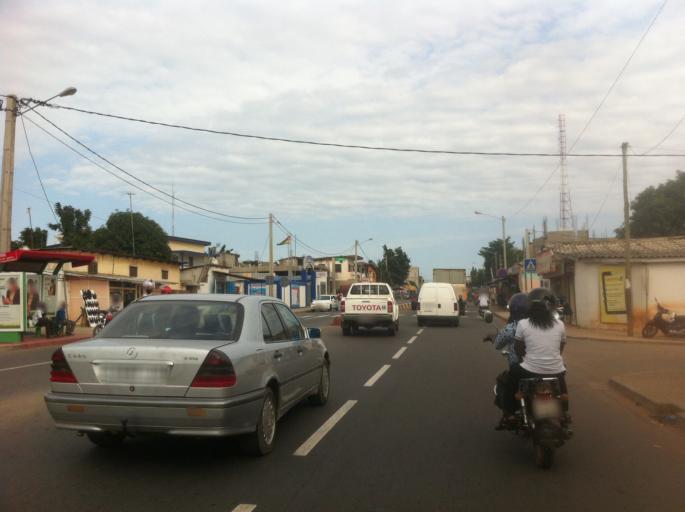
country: TG
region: Maritime
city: Lome
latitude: 6.1476
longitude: 1.2028
